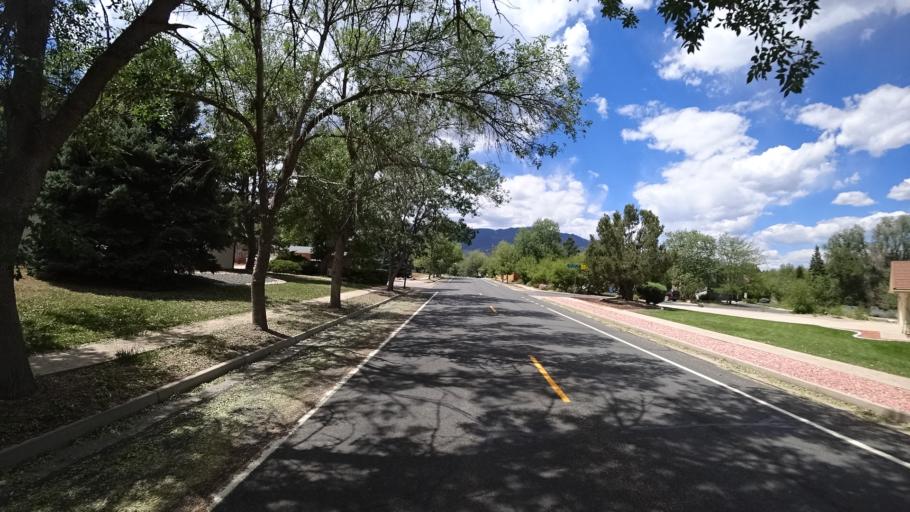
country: US
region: Colorado
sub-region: El Paso County
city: Colorado Springs
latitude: 38.7913
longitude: -104.8310
